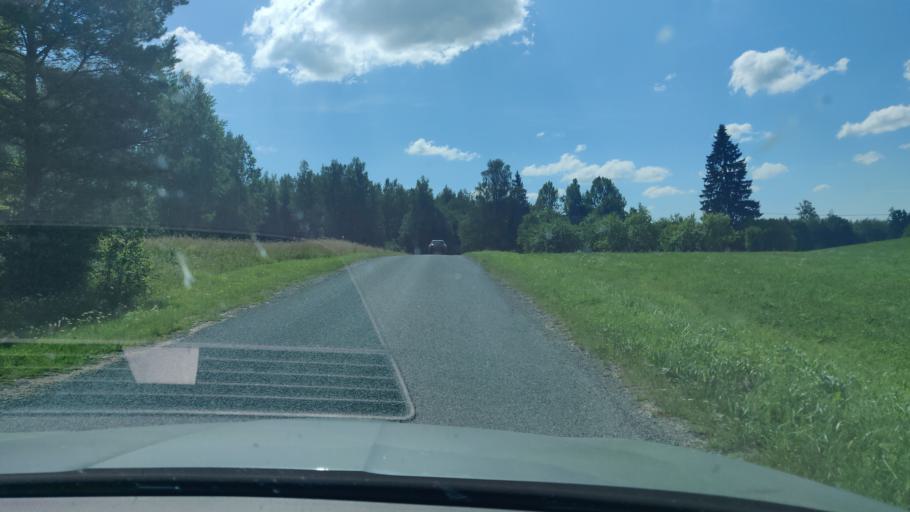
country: EE
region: Tartu
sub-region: Elva linn
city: Elva
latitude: 58.1597
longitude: 26.4700
